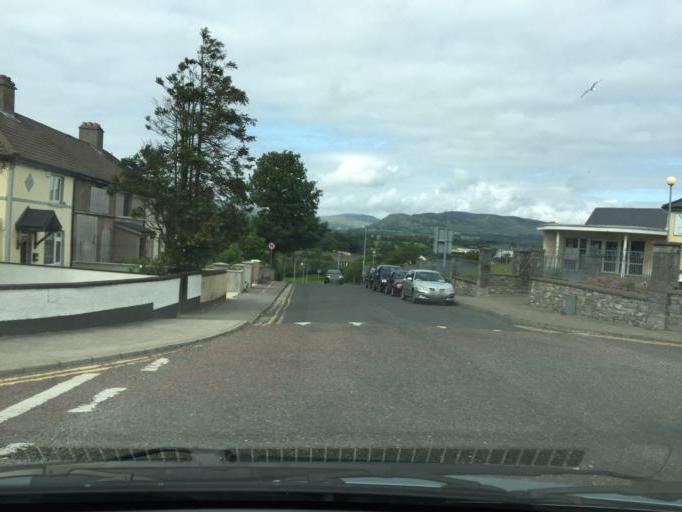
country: IE
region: Connaught
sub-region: Sligo
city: Sligo
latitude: 54.2761
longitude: -8.4724
